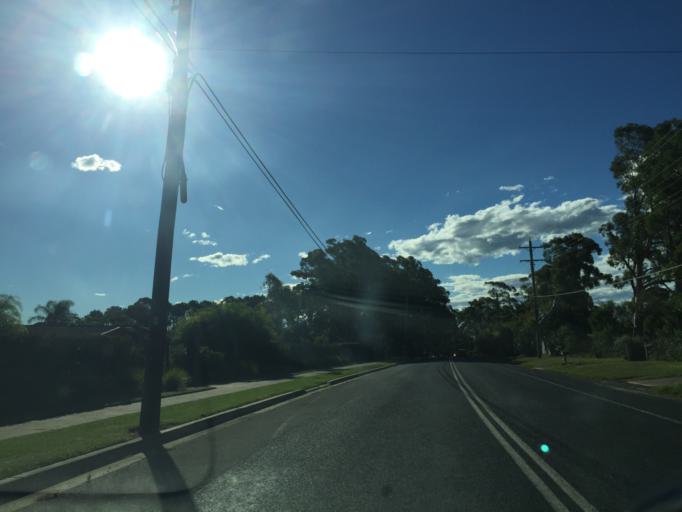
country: AU
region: New South Wales
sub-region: The Hills Shire
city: Glenhaven
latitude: -33.6965
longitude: 150.9894
